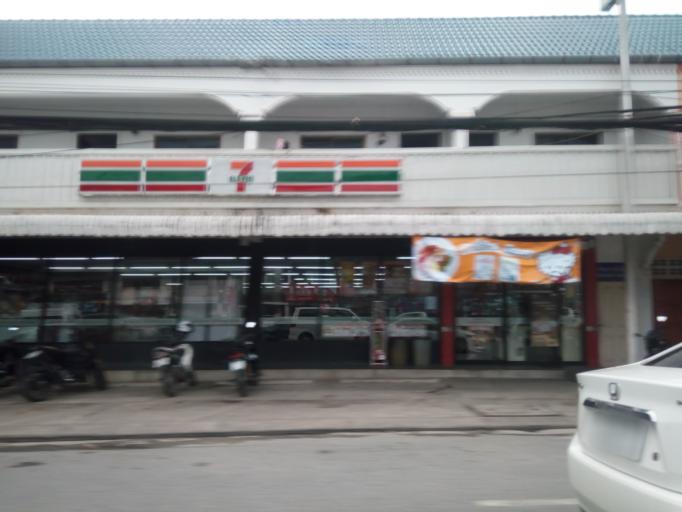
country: TH
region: Phuket
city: Thalang
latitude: 8.0281
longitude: 98.3330
